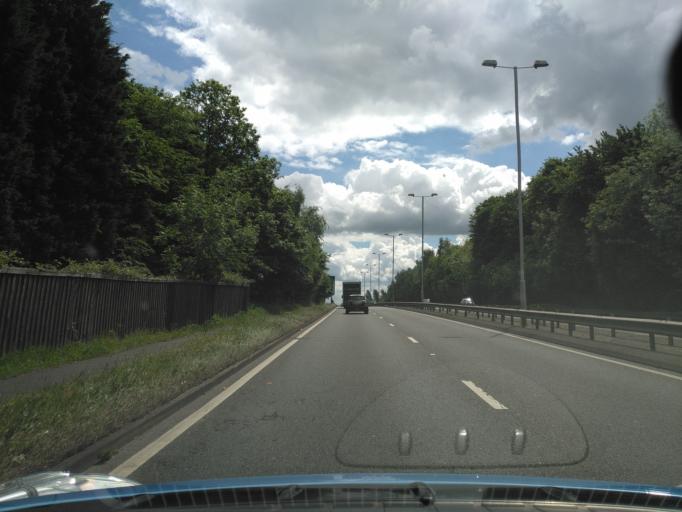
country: GB
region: England
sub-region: Greater London
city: Sidcup
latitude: 51.4229
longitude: 0.0914
